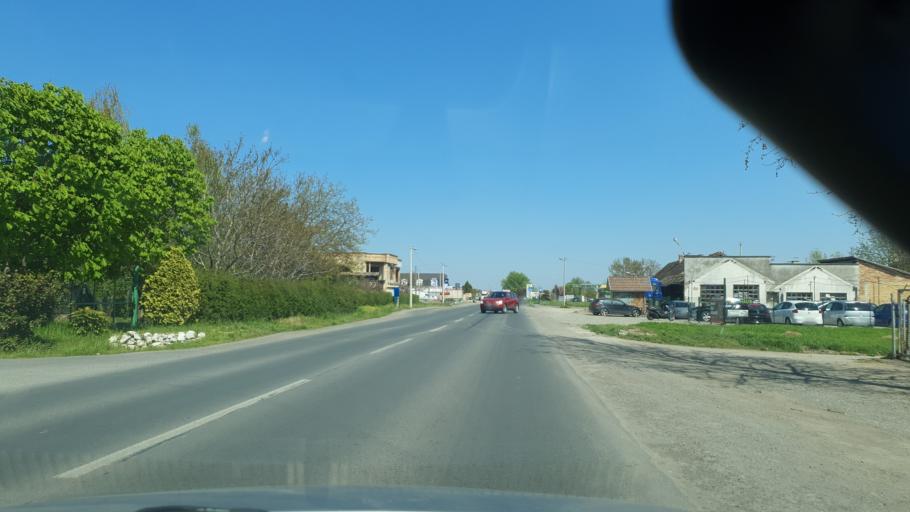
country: RS
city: Veternik
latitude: 45.2441
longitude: 19.7262
